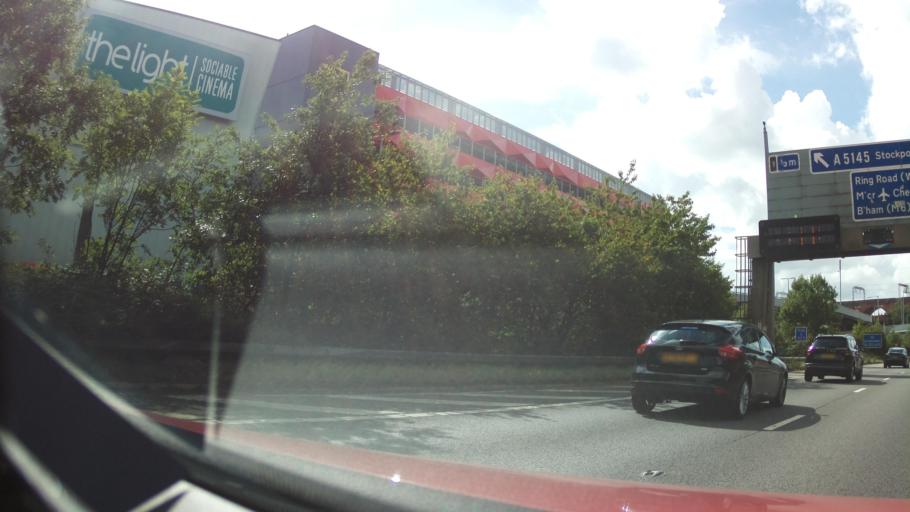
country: GB
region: England
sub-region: Borough of Stockport
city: Stockport
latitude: 53.4124
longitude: -2.1623
